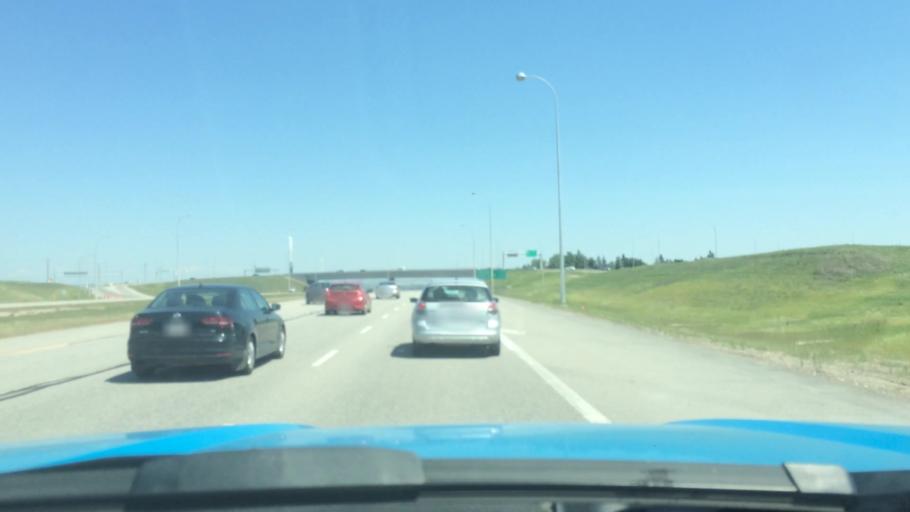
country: CA
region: Alberta
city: Calgary
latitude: 51.1513
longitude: -114.1718
